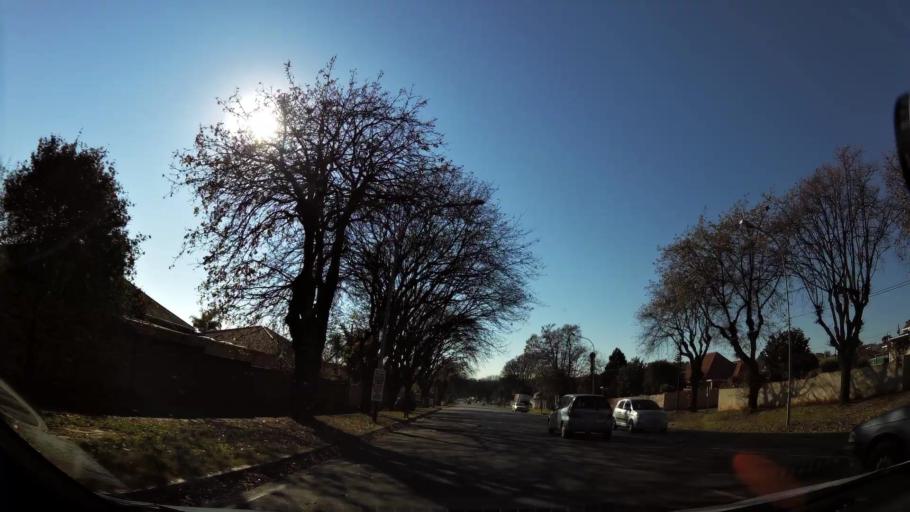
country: ZA
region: Gauteng
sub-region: City of Johannesburg Metropolitan Municipality
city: Johannesburg
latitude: -26.1961
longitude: 28.0941
